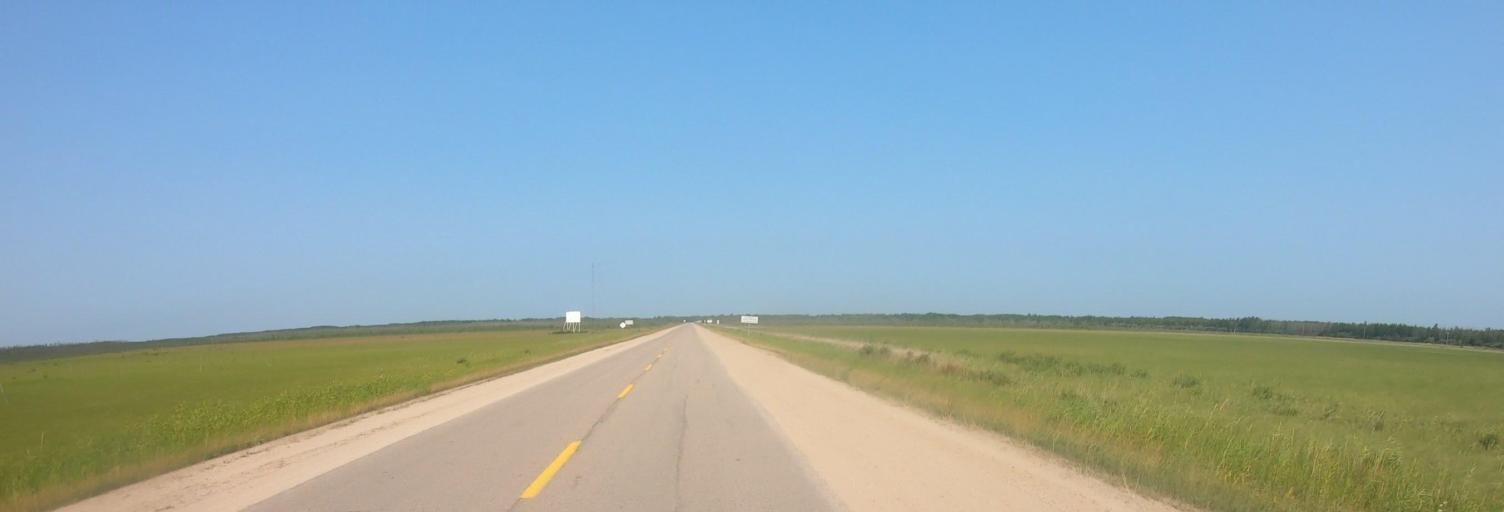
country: US
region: Minnesota
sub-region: Roseau County
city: Warroad
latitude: 49.0079
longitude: -95.3850
